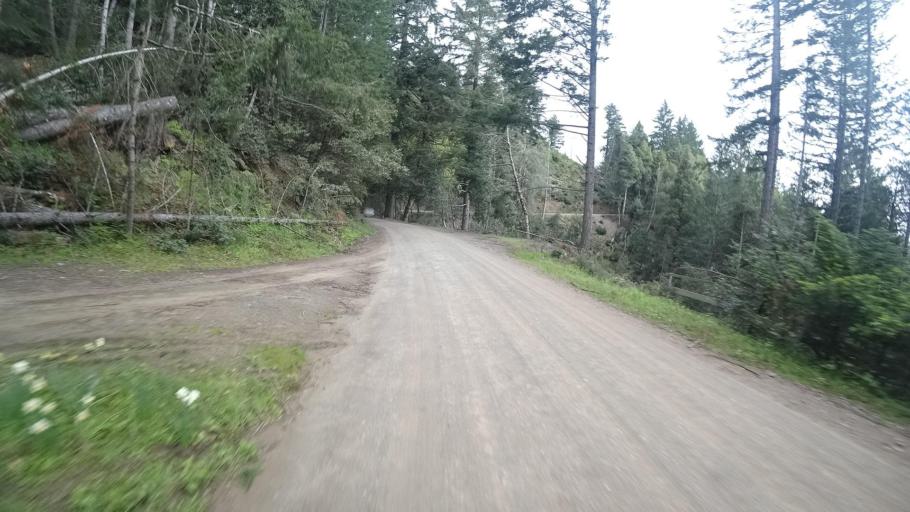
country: US
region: California
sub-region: Humboldt County
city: Redway
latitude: 40.2610
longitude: -123.7683
